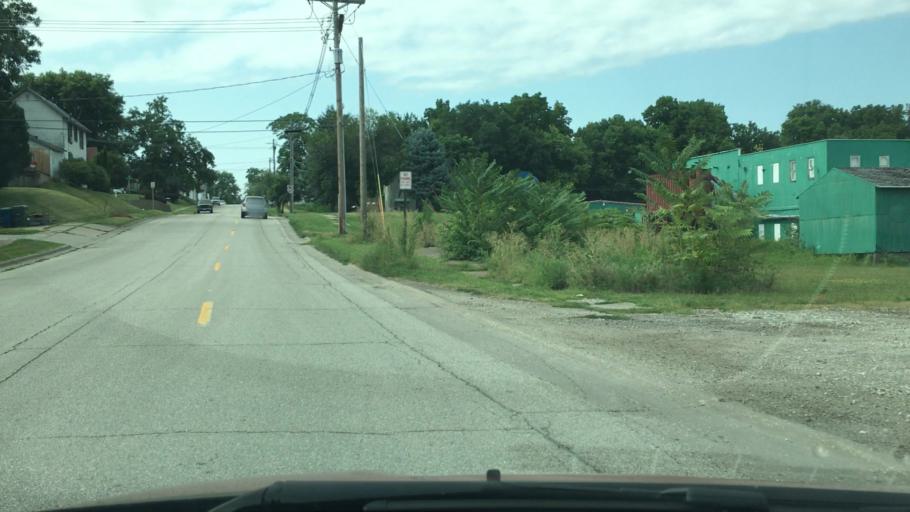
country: US
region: Iowa
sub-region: Muscatine County
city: Muscatine
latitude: 41.4291
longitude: -91.0386
